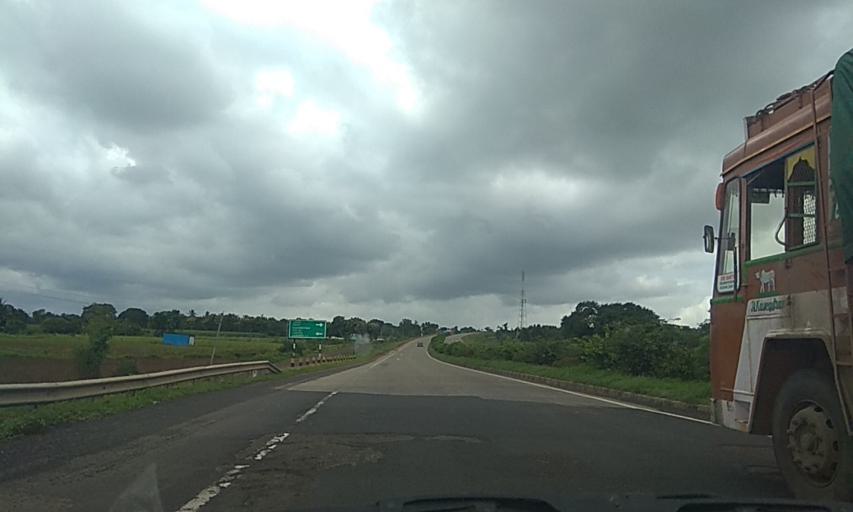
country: IN
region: Karnataka
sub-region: Belgaum
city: Sankeshwar
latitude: 16.2509
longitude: 74.4757
